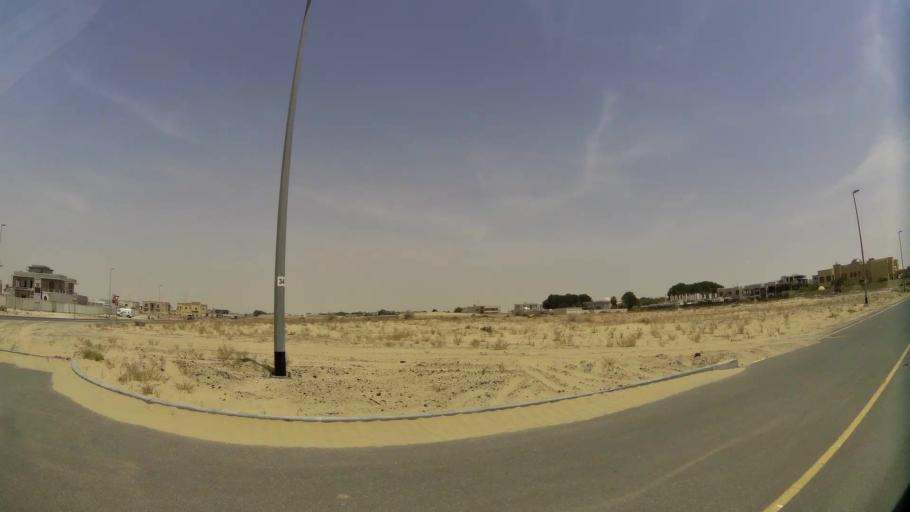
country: AE
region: Ash Shariqah
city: Sharjah
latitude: 25.2417
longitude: 55.4887
